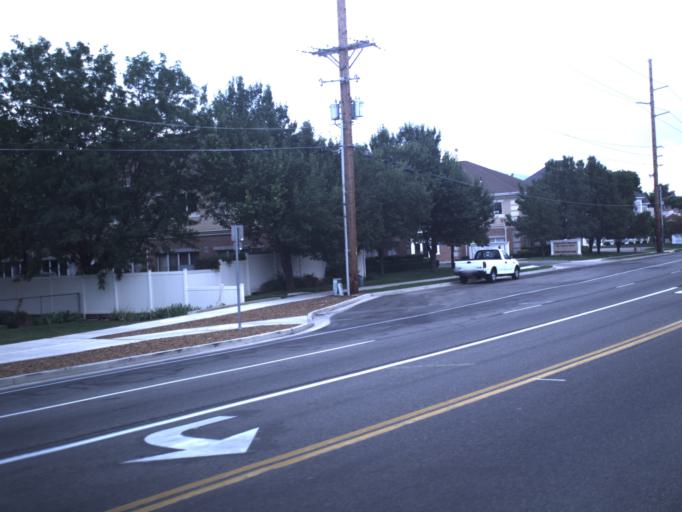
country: US
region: Utah
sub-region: Salt Lake County
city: Murray
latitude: 40.6594
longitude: -111.8660
